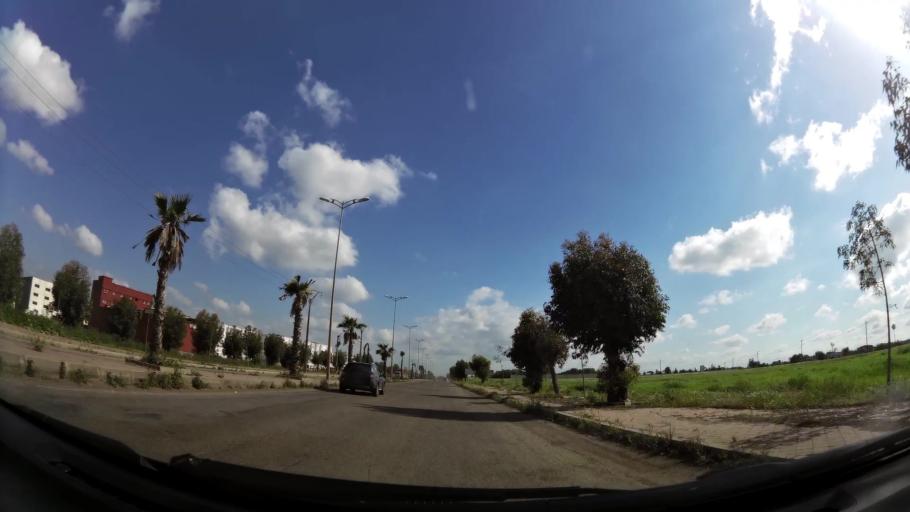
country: MA
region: Grand Casablanca
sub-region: Mediouna
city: Mediouna
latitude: 33.4457
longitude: -7.5209
